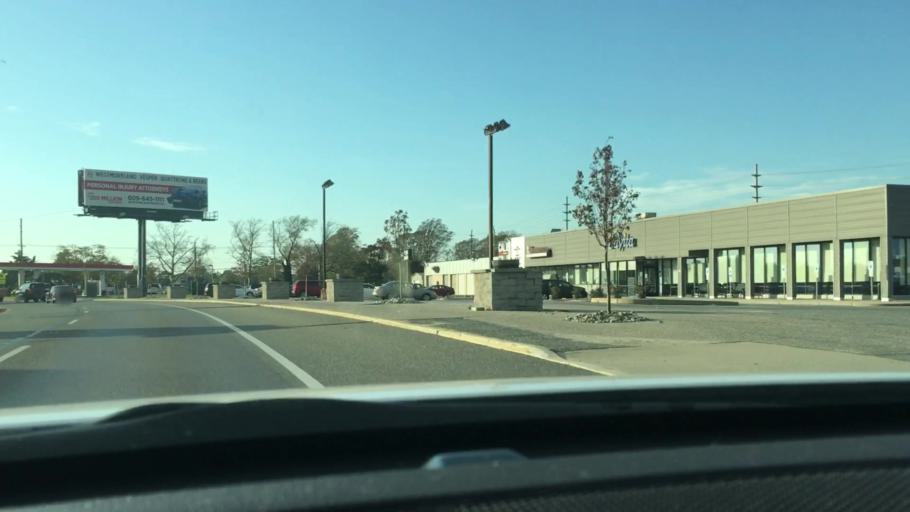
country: US
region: New Jersey
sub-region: Atlantic County
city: Pleasantville
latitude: 39.3917
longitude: -74.5283
